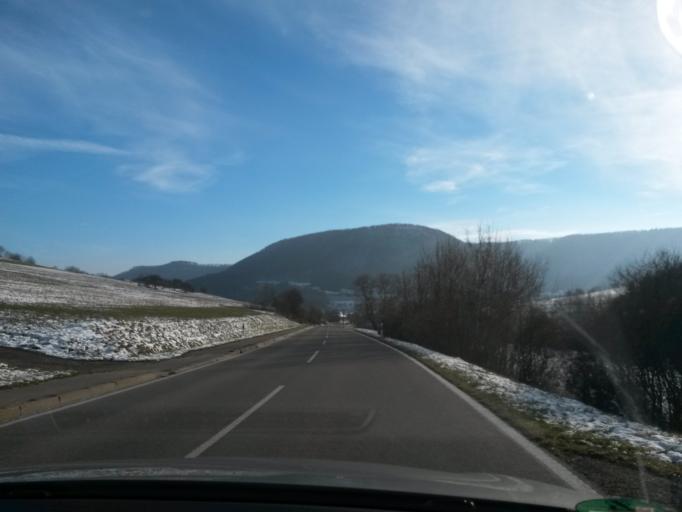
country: DE
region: Baden-Wuerttemberg
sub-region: Regierungsbezirk Stuttgart
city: Bad Uberkingen
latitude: 48.6151
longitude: 9.7596
